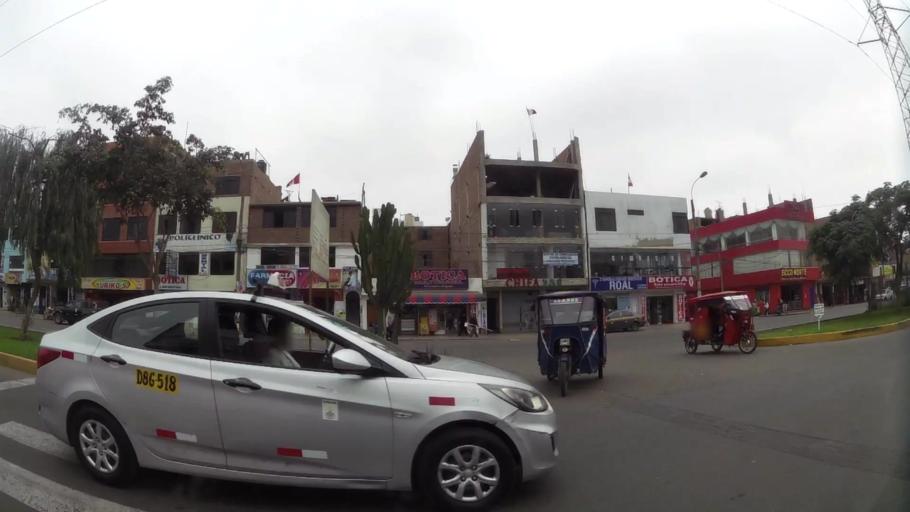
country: PE
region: Lima
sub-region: Lima
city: Independencia
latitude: -11.9709
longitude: -77.0779
